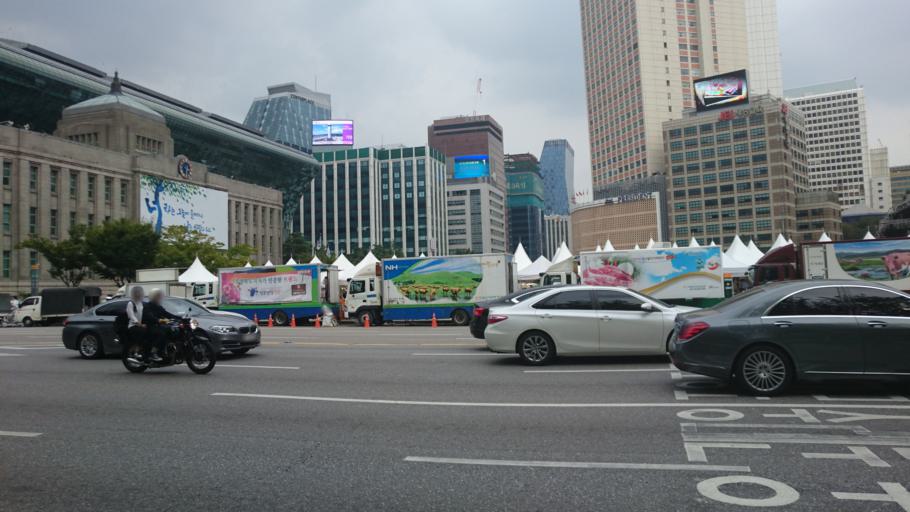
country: KR
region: Seoul
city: Seoul
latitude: 37.5656
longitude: 126.9772
